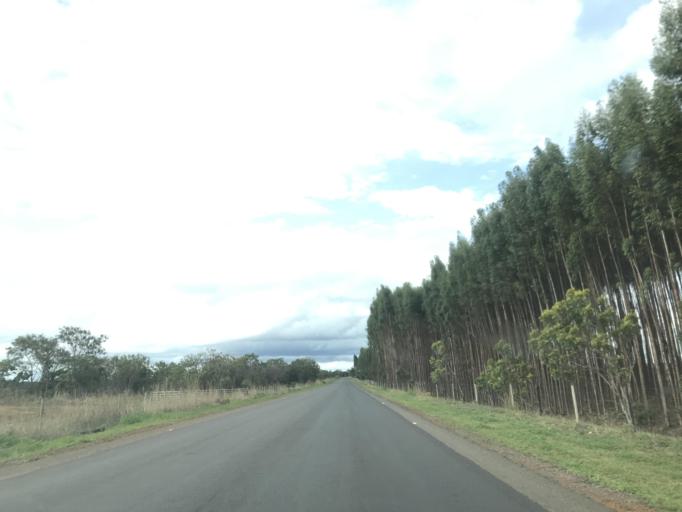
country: BR
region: Goias
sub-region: Bela Vista De Goias
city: Bela Vista de Goias
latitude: -16.9892
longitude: -48.6691
